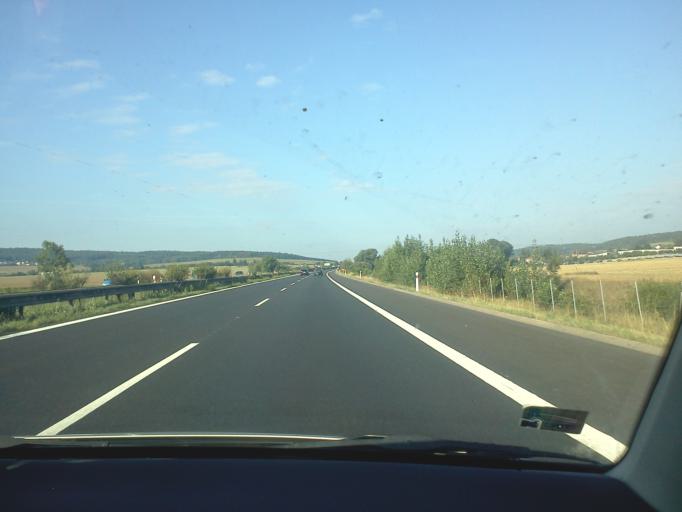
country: CZ
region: Central Bohemia
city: Komarov
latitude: 49.8477
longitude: 13.8517
